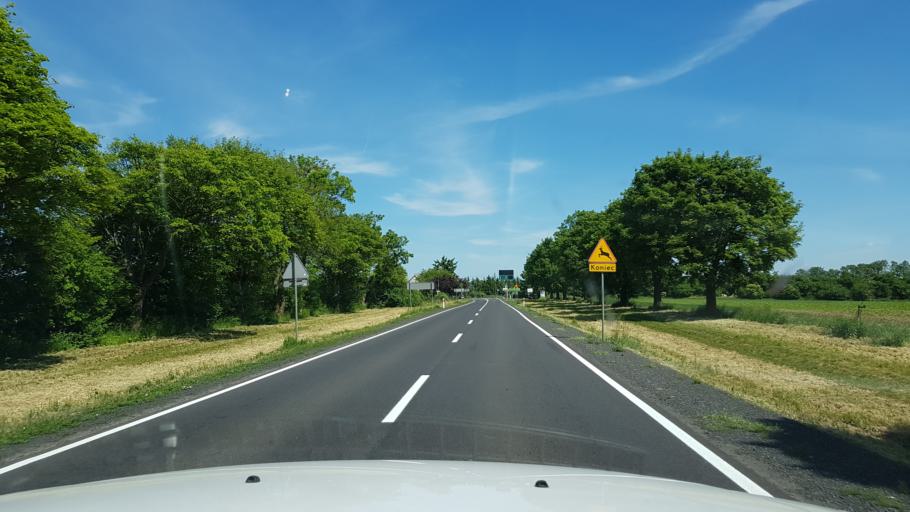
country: PL
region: West Pomeranian Voivodeship
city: Trzcinsko Zdroj
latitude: 52.9621
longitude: 14.5885
